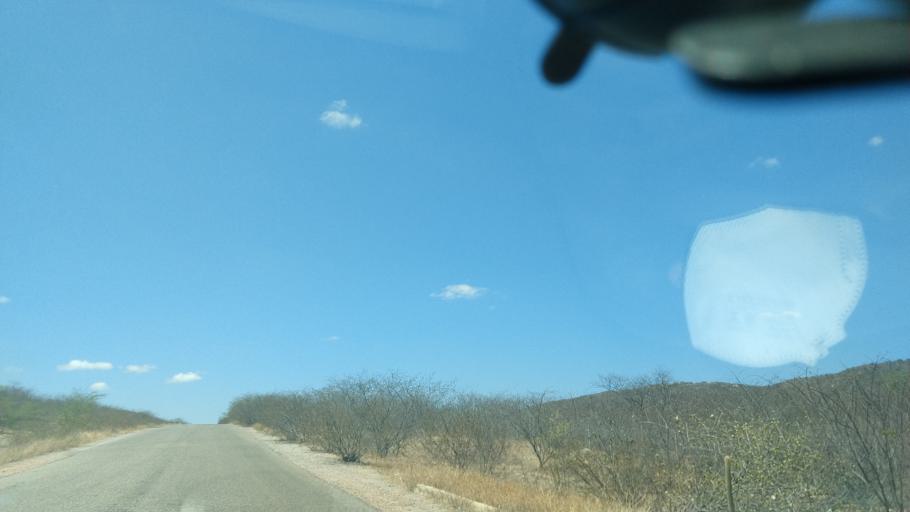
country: BR
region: Rio Grande do Norte
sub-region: Sao Tome
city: Sao Tome
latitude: -5.9705
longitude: -36.1332
